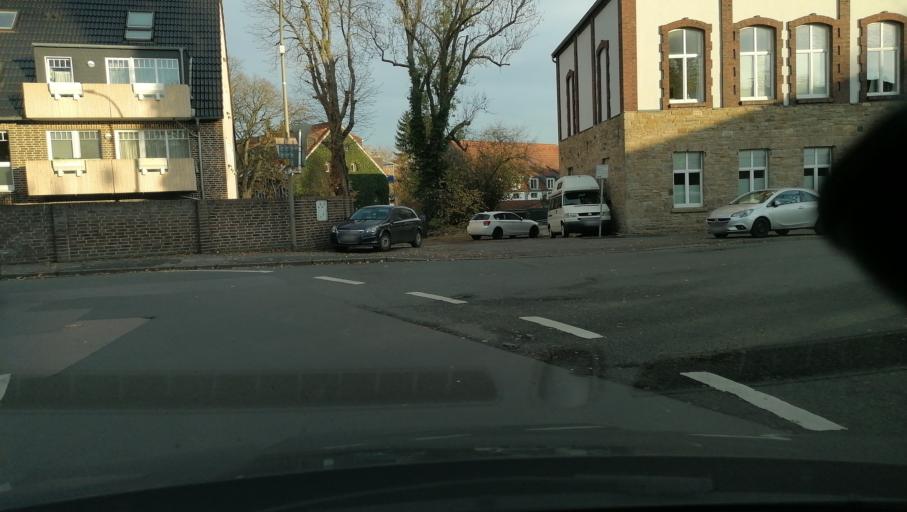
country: DE
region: North Rhine-Westphalia
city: Schwerte
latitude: 51.4953
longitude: 7.5321
